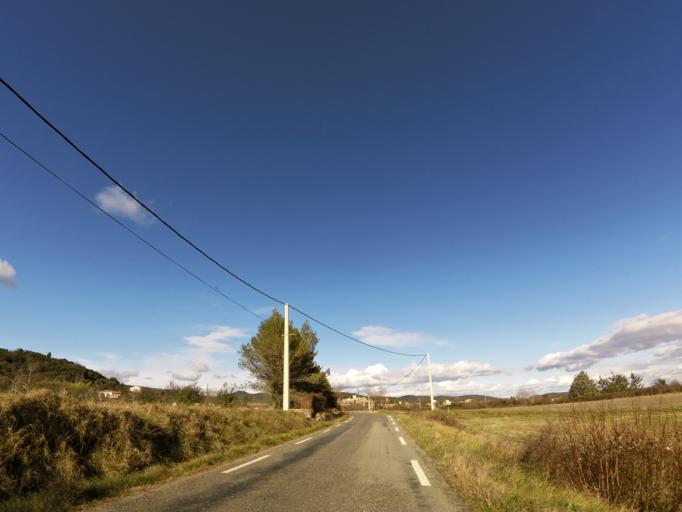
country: FR
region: Languedoc-Roussillon
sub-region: Departement du Gard
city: Sauve
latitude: 43.9836
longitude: 3.9509
